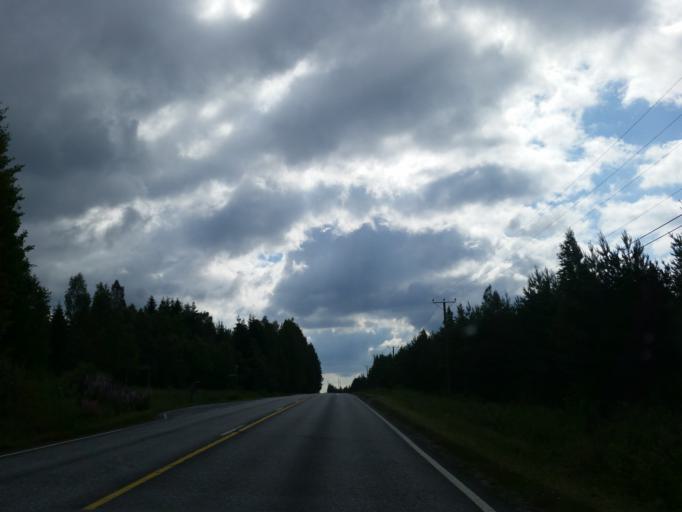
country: FI
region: Northern Savo
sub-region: Kuopio
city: Kuopio
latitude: 62.8445
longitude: 27.4675
